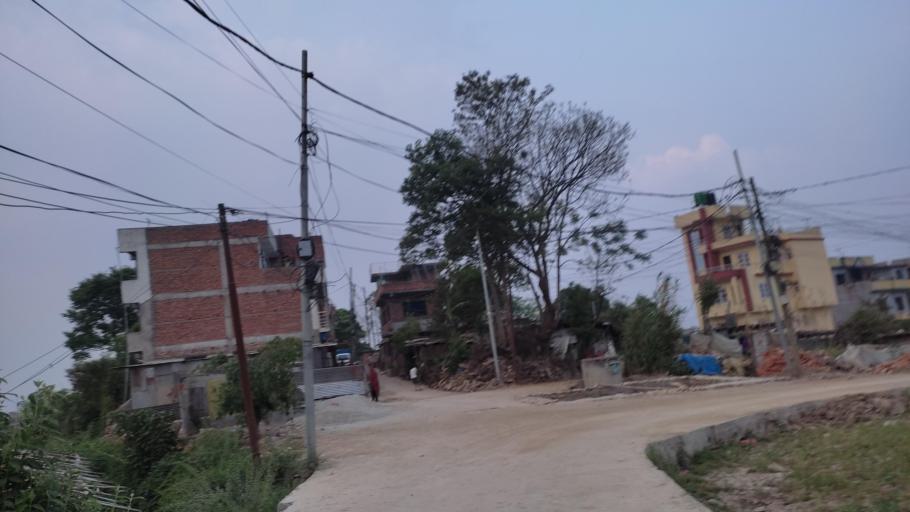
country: NP
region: Central Region
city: Kirtipur
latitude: 27.6709
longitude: 85.2646
